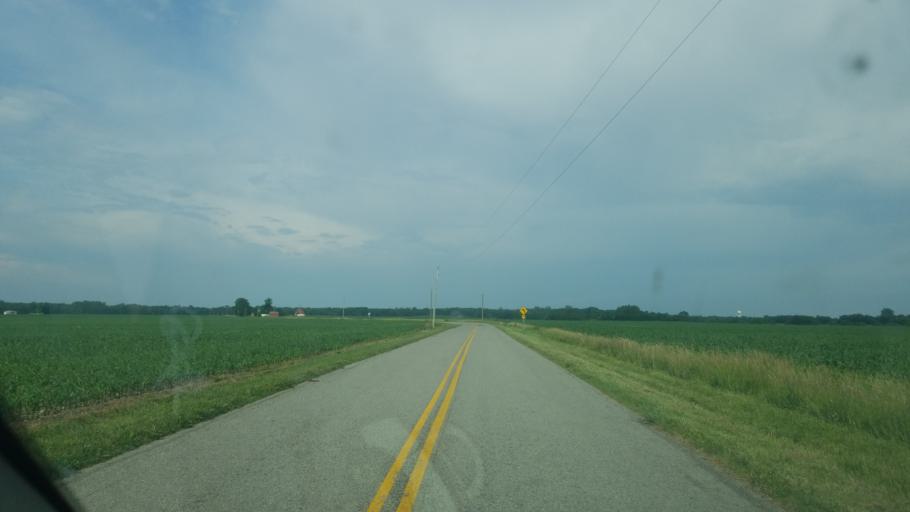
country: US
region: Ohio
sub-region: Champaign County
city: North Lewisburg
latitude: 40.1812
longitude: -83.4722
